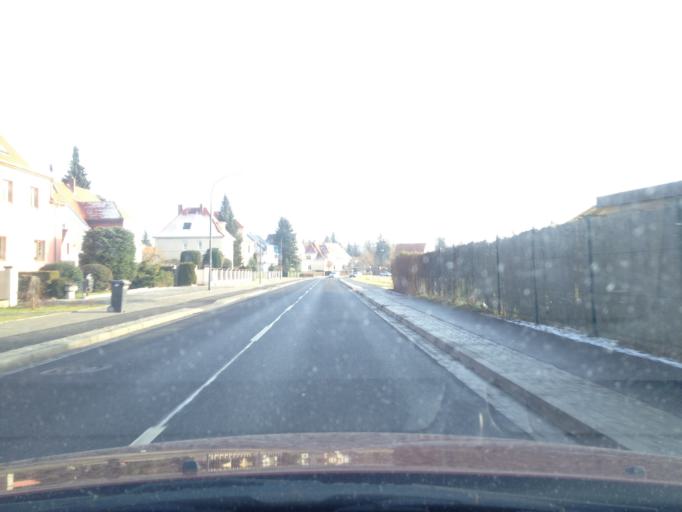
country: DE
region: Saxony
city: Goerlitz
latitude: 51.1393
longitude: 14.9497
